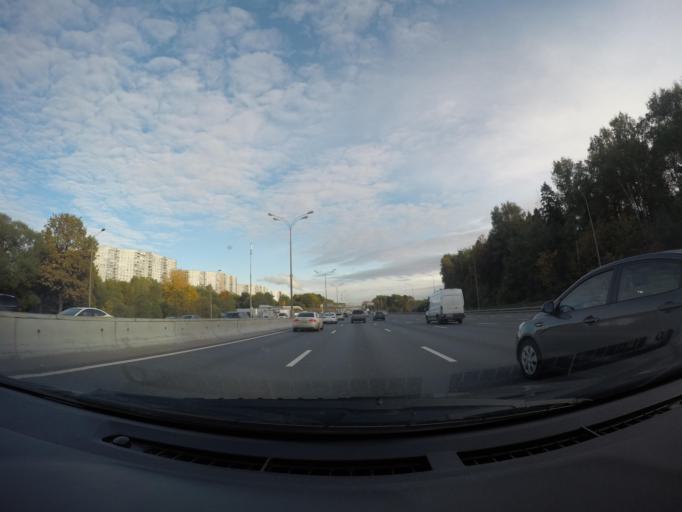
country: RU
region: Moscow
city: Yasenevo
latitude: 55.5909
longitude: 37.5312
